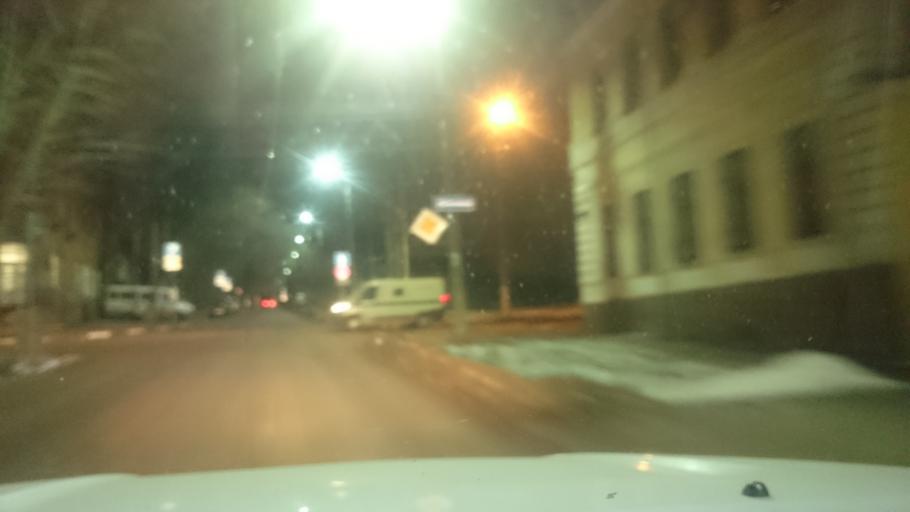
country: RU
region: Tula
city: Tula
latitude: 54.1838
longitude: 37.6153
